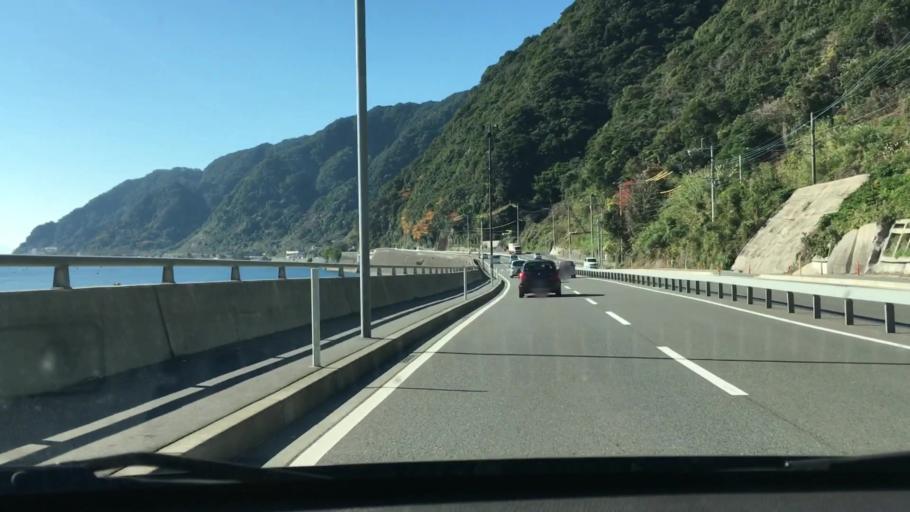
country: JP
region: Kagoshima
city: Kajiki
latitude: 31.6548
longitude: 130.6106
